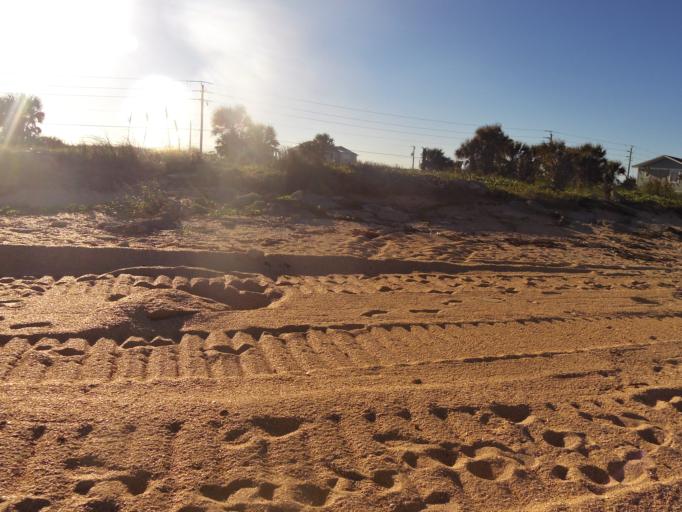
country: US
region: Florida
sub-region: Flagler County
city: Palm Coast
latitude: 29.6599
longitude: -81.2086
